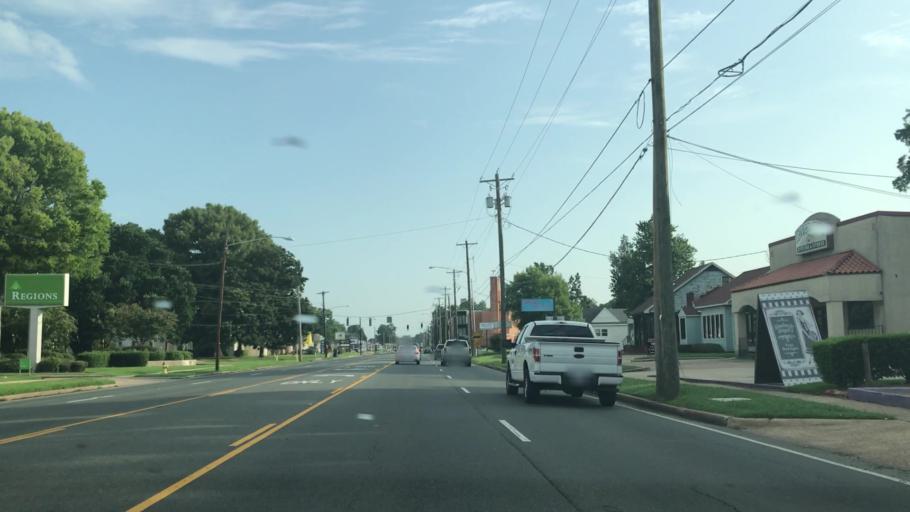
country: US
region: Louisiana
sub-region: Bossier Parish
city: Bossier City
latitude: 32.4694
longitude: -93.7221
